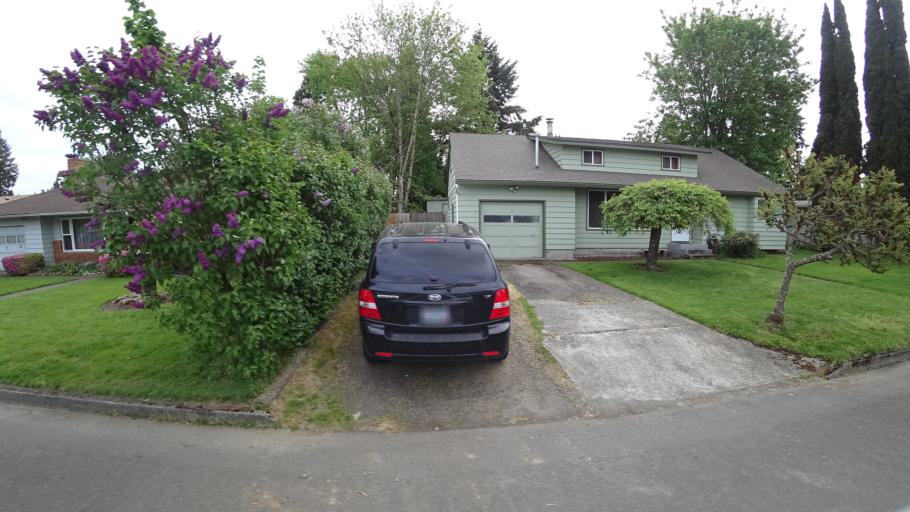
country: US
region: Oregon
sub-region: Washington County
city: Hillsboro
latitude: 45.5262
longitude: -122.9950
